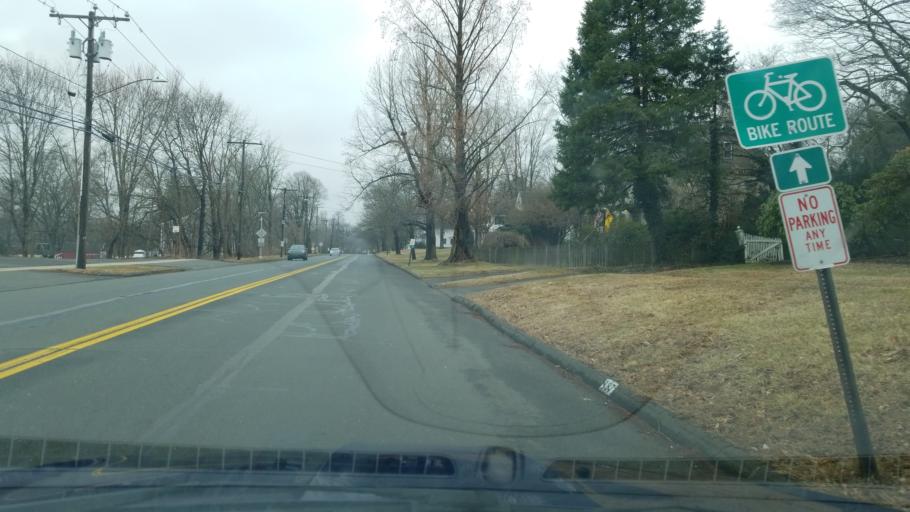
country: US
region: Connecticut
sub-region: Hartford County
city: Wethersfield
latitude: 41.6877
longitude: -72.6718
